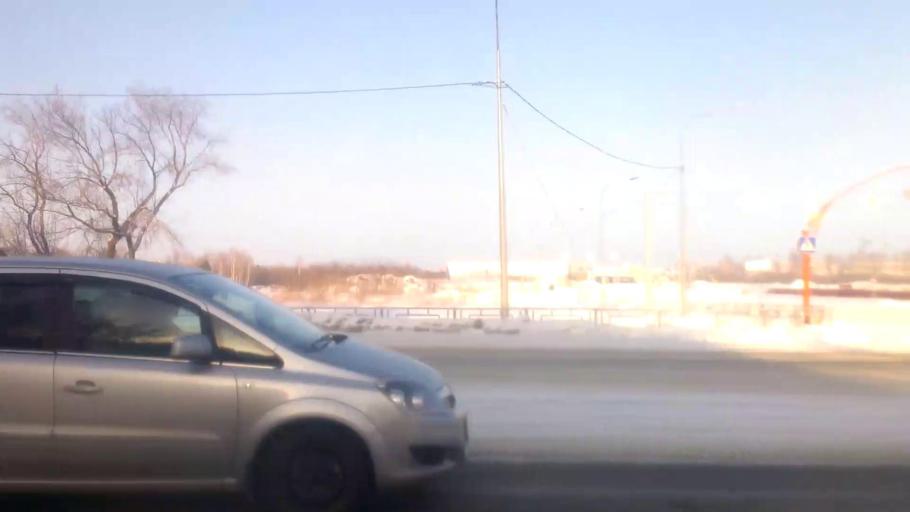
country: RU
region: Altai Krai
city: Novosilikatnyy
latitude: 53.3465
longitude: 83.6495
